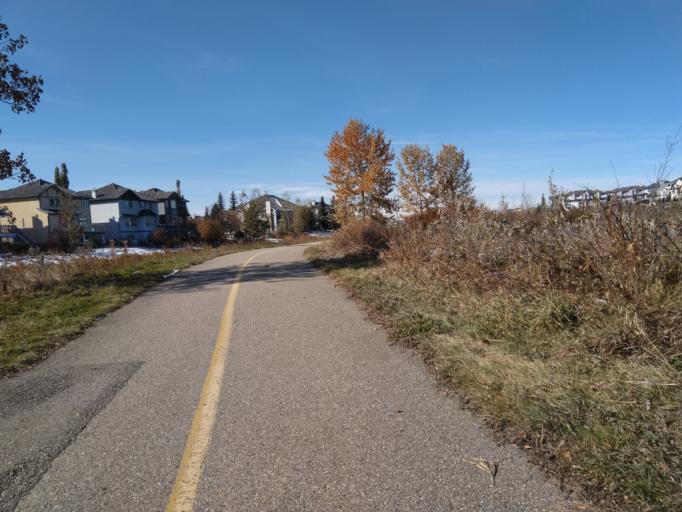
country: CA
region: Alberta
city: Calgary
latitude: 51.1558
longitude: -114.1034
